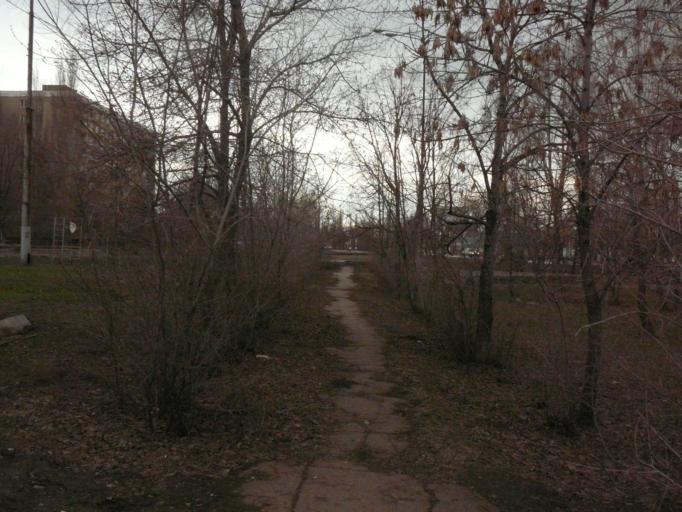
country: RU
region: Saratov
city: Engel's
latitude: 51.4693
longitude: 46.1148
